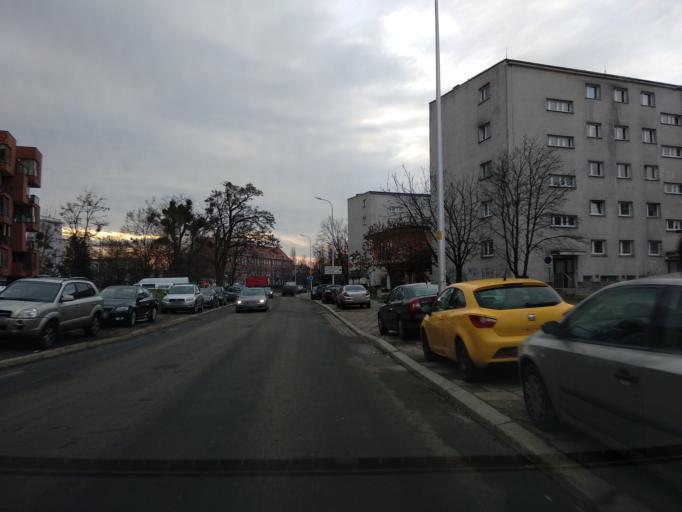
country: PL
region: Lower Silesian Voivodeship
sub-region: Powiat wroclawski
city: Wroclaw
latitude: 51.0958
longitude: 16.9867
